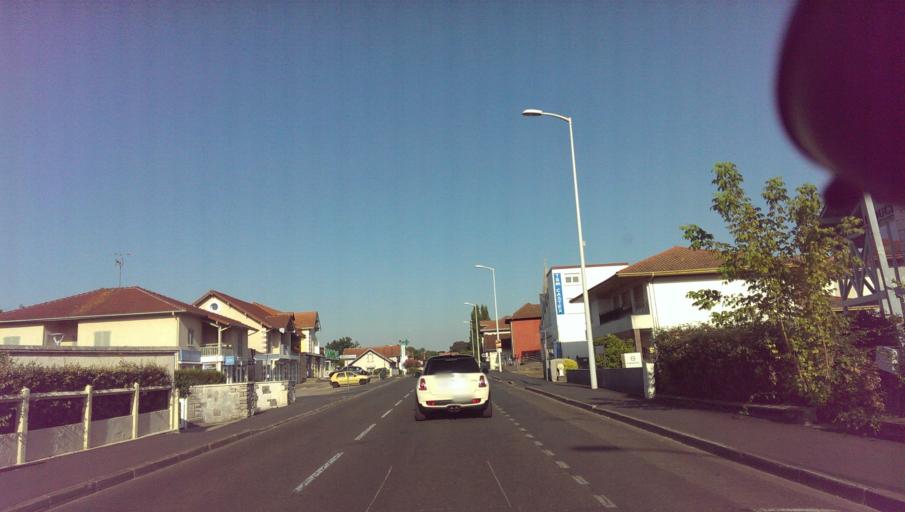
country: FR
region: Aquitaine
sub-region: Departement des Landes
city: Mimizan
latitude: 44.2028
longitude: -1.2321
